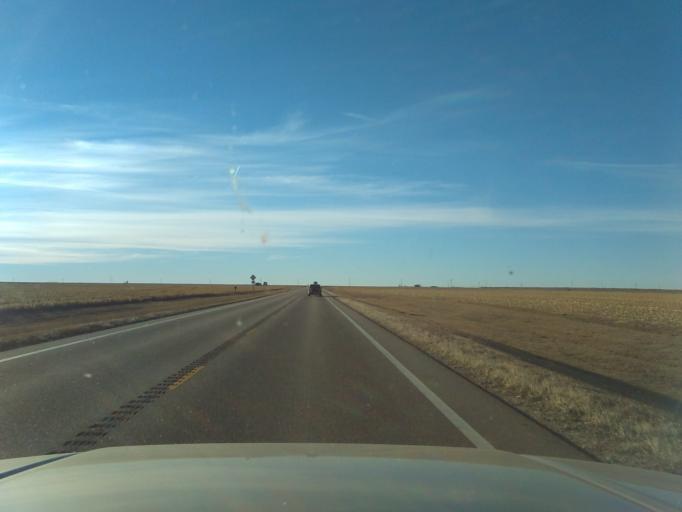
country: US
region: Kansas
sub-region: Thomas County
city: Colby
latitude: 39.4649
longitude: -100.7466
